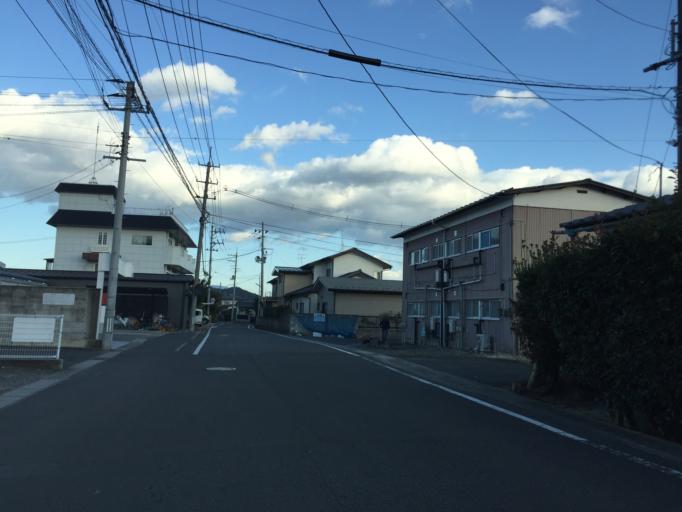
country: JP
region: Fukushima
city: Fukushima-shi
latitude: 37.8062
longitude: 140.4861
